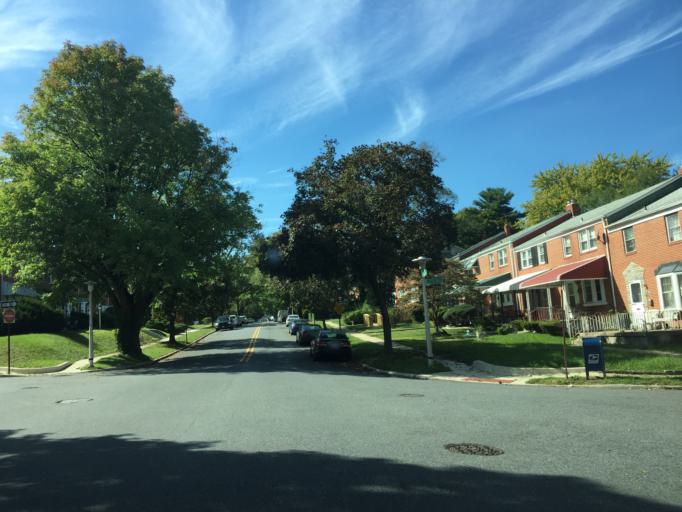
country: US
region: Maryland
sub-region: Baltimore County
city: Towson
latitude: 39.3711
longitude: -76.5891
